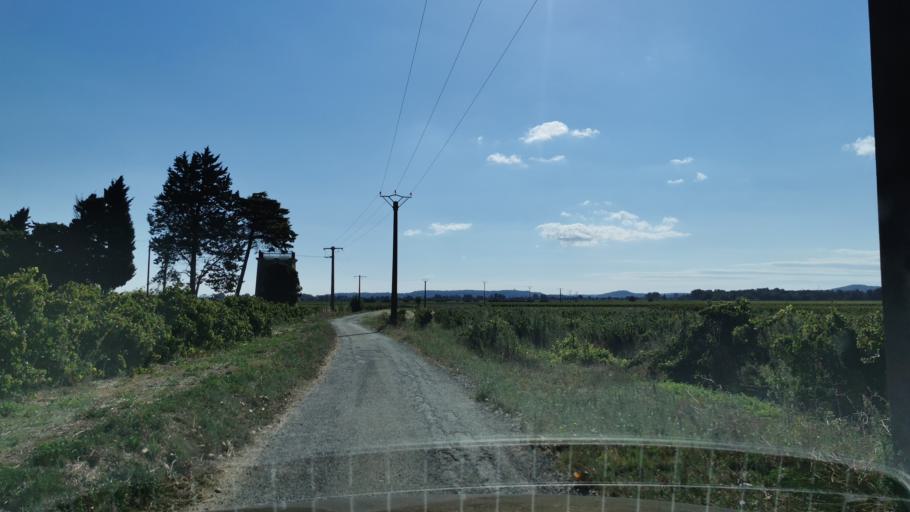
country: FR
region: Languedoc-Roussillon
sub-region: Departement de l'Aude
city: Canet
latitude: 43.2451
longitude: 2.8585
